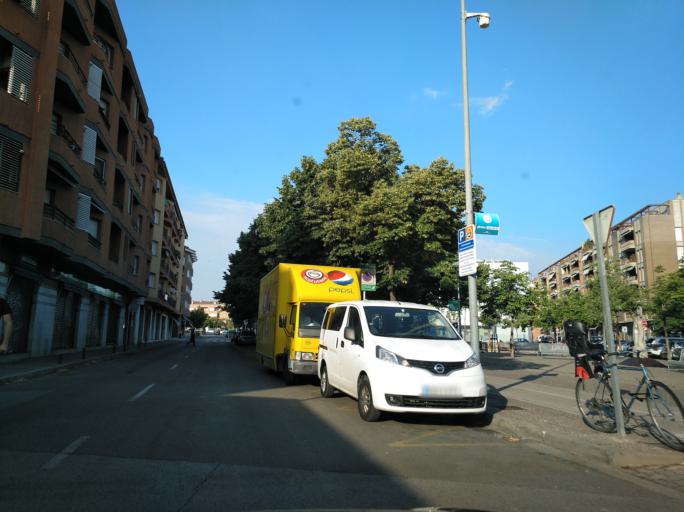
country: ES
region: Catalonia
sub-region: Provincia de Girona
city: Girona
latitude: 41.9841
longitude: 2.8162
